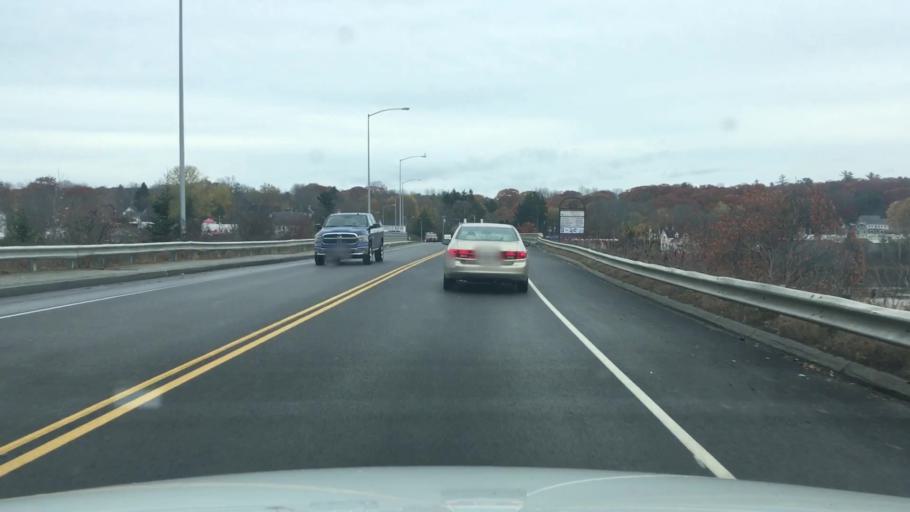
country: US
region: Maine
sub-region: Hancock County
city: Bucksport
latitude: 44.5680
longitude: -68.7892
